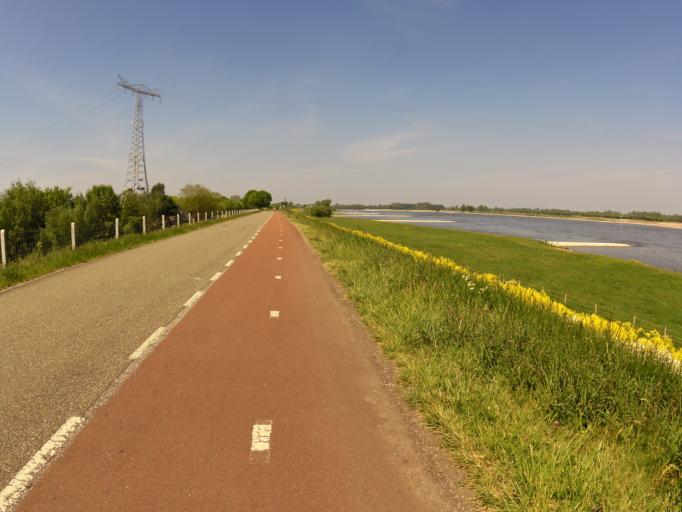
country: NL
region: Gelderland
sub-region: Gemeente Neerijnen
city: Neerijnen
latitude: 51.8077
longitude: 5.3312
